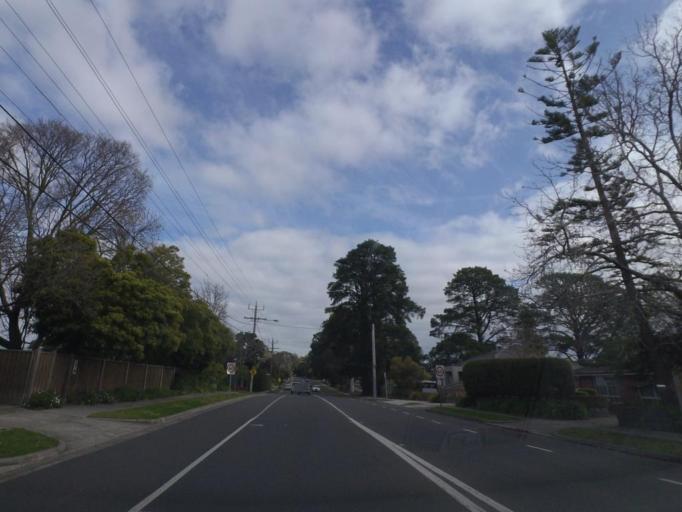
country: AU
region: Victoria
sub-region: Maroondah
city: Warranwood
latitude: -37.7950
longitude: 145.2407
